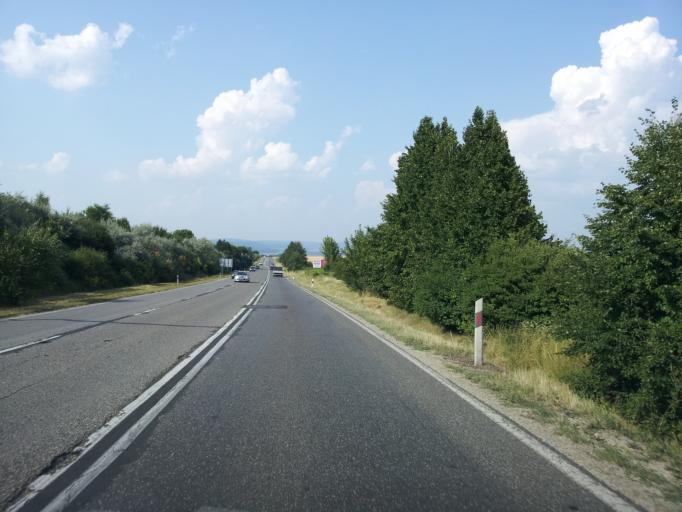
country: HU
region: Veszprem
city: Veszprem
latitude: 47.0880
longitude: 17.9311
